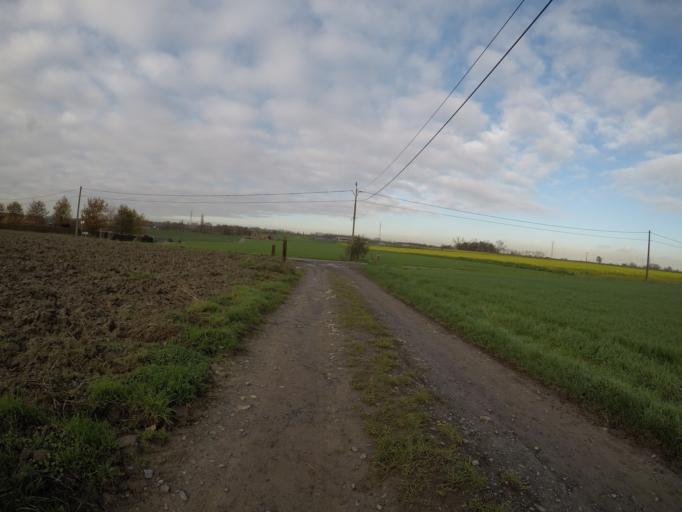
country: BE
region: Flanders
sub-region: Provincie West-Vlaanderen
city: Wervik
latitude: 50.8214
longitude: 3.0095
